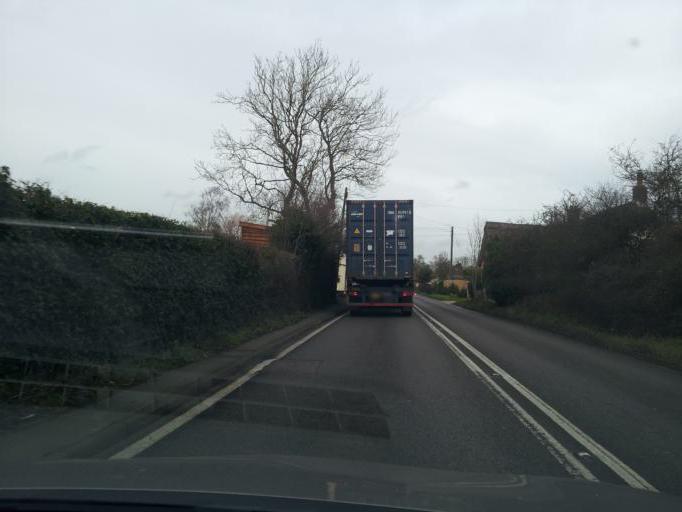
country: GB
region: England
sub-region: Suffolk
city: Needham Market
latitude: 52.1951
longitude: 1.0980
